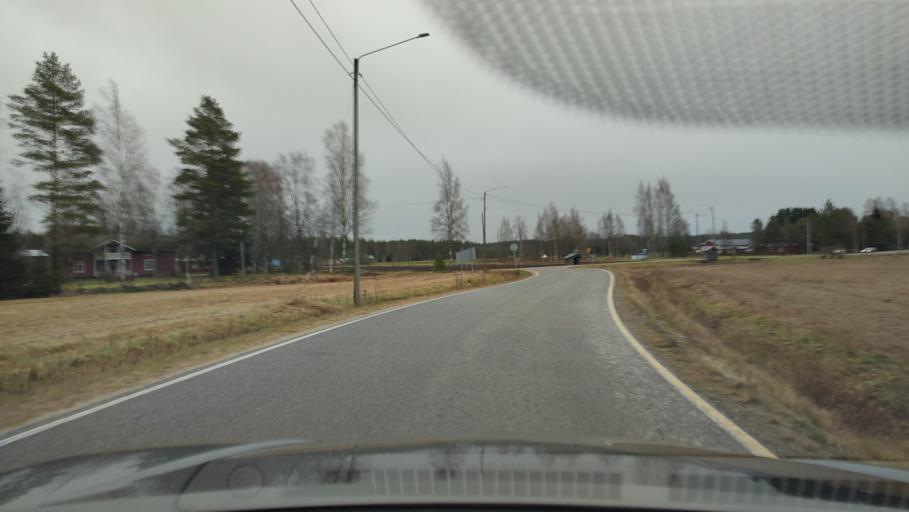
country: FI
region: Southern Ostrobothnia
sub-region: Suupohja
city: Isojoki
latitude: 62.1906
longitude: 21.9810
